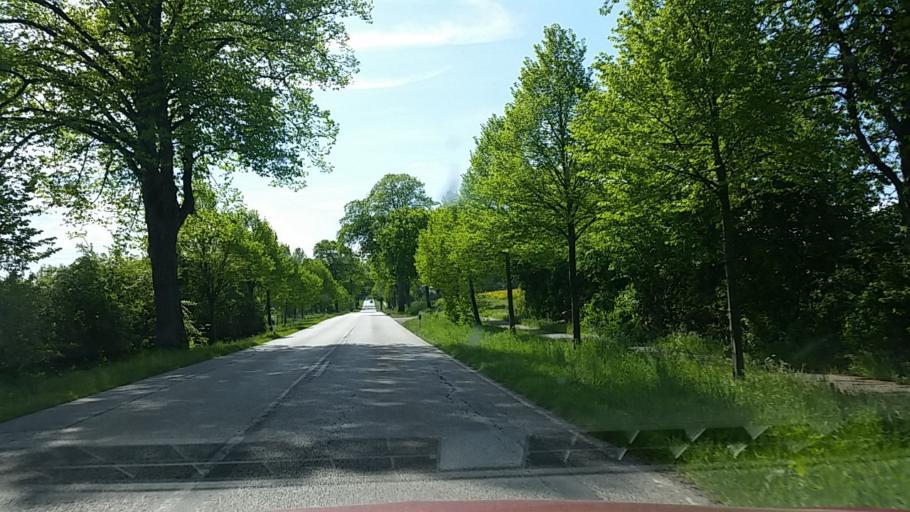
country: DE
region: Schleswig-Holstein
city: Hamberge
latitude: 53.8496
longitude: 10.6233
